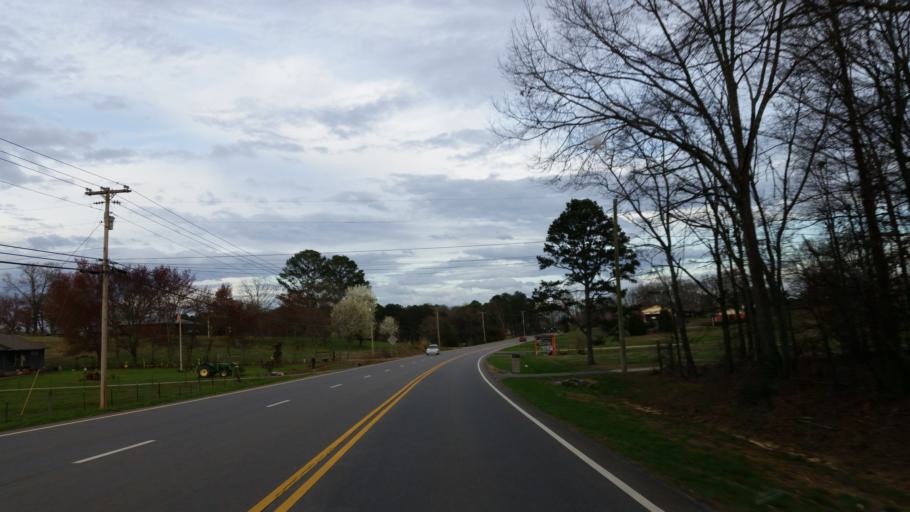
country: US
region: Georgia
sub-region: Gordon County
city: Calhoun
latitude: 34.4526
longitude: -84.8754
